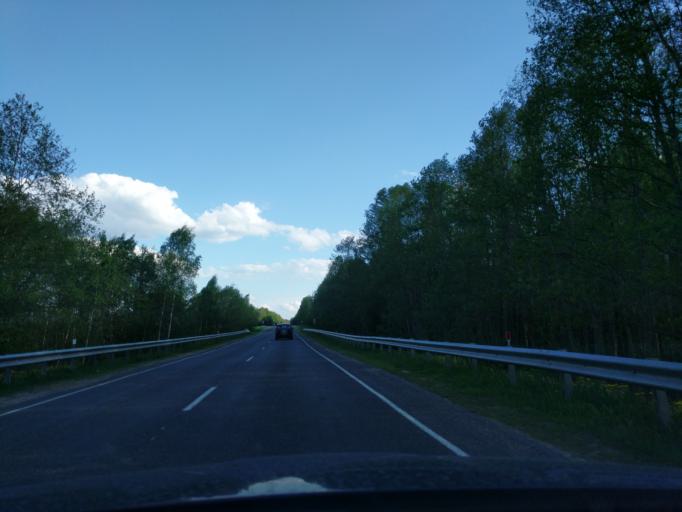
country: BY
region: Minsk
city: Kryvichy
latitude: 54.6091
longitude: 27.1797
